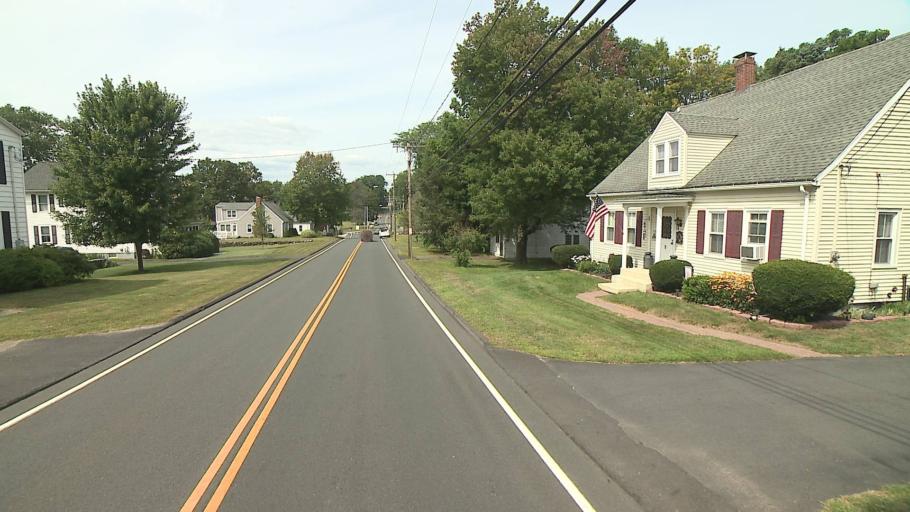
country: US
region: Connecticut
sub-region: Litchfield County
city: Plymouth
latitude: 41.6706
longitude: -73.0525
